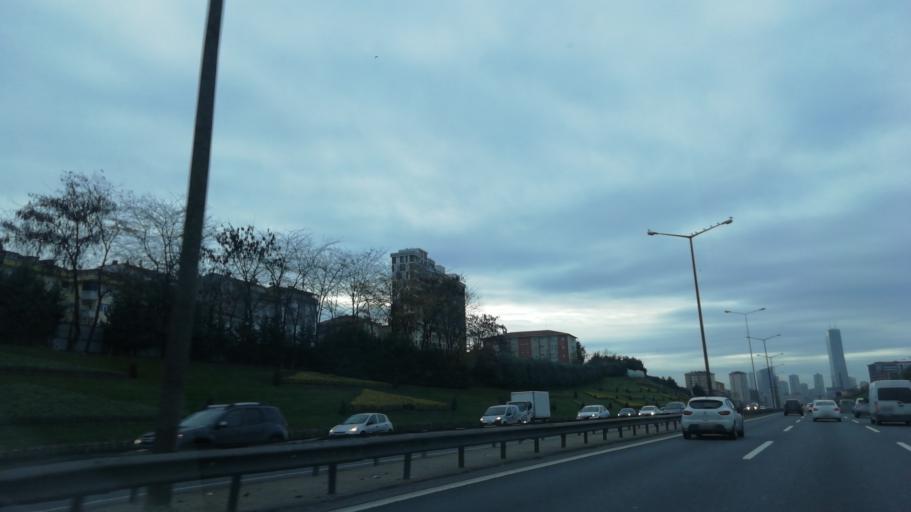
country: TR
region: Istanbul
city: Umraniye
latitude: 41.0202
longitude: 29.1207
